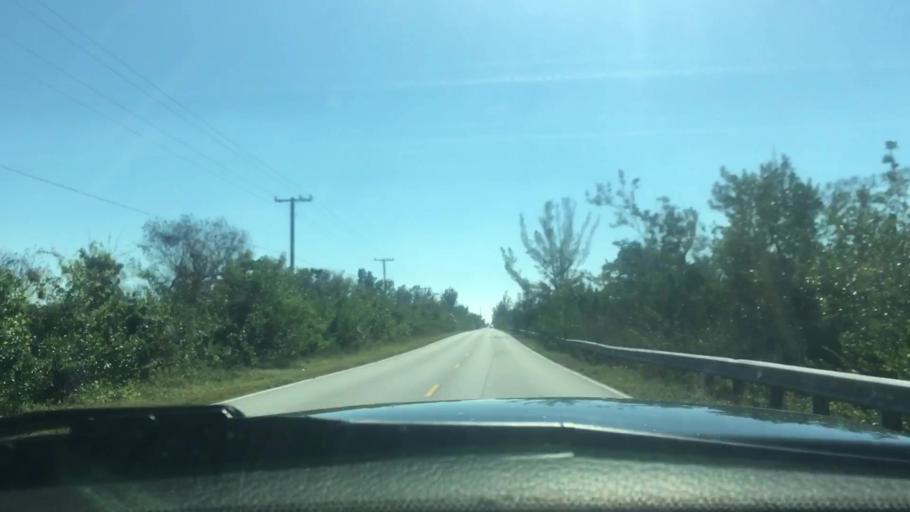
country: US
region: Florida
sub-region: Miami-Dade County
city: Florida City
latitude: 25.3698
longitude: -80.4317
